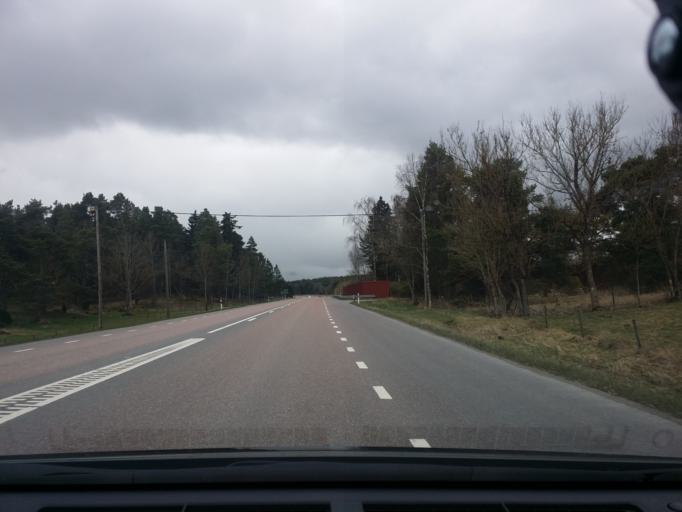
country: SE
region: Uppsala
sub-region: Enkopings Kommun
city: Irsta
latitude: 59.7315
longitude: 16.9578
